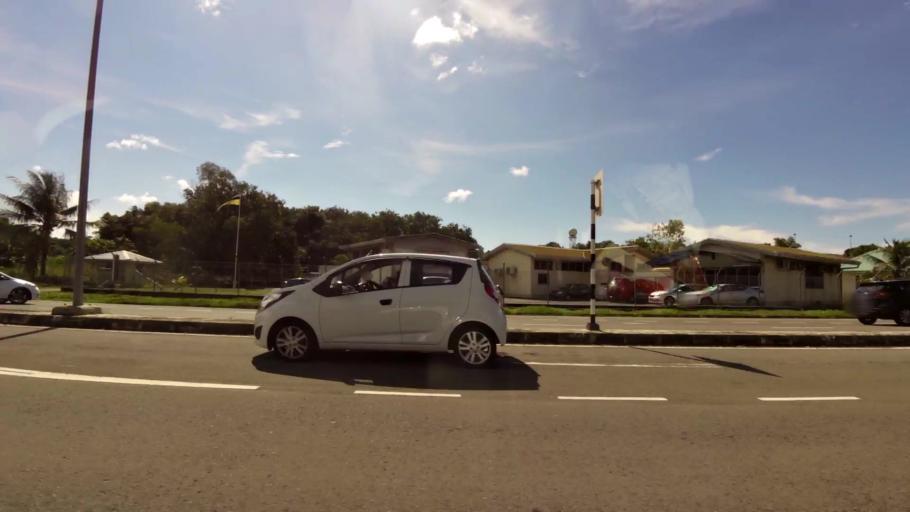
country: BN
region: Brunei and Muara
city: Bandar Seri Begawan
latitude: 4.9489
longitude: 114.9432
